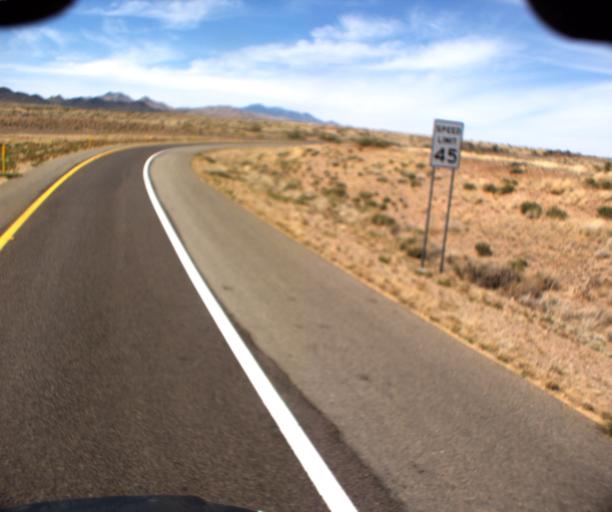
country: US
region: Arizona
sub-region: Cochise County
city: Willcox
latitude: 32.3909
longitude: -109.6630
